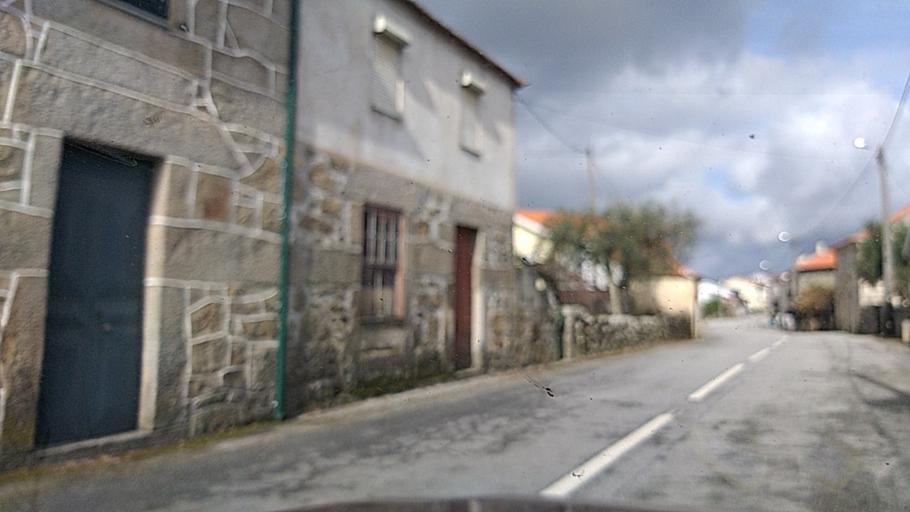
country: PT
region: Guarda
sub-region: Fornos de Algodres
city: Fornos de Algodres
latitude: 40.6496
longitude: -7.5472
